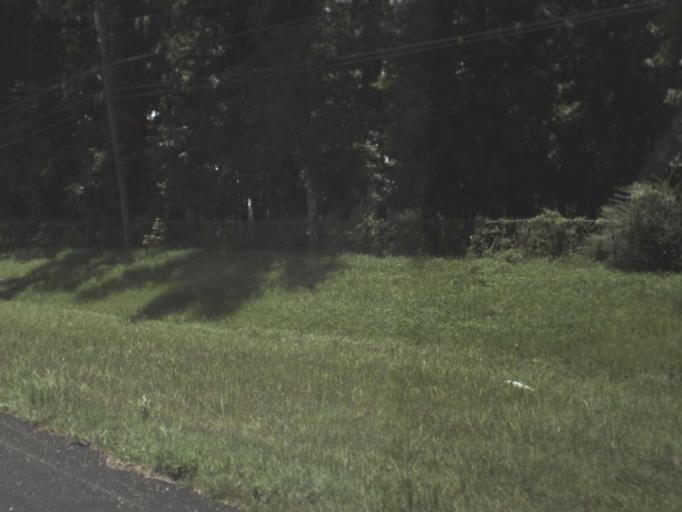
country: US
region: Florida
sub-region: Hernando County
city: Hill 'n Dale
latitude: 28.5354
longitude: -82.3373
